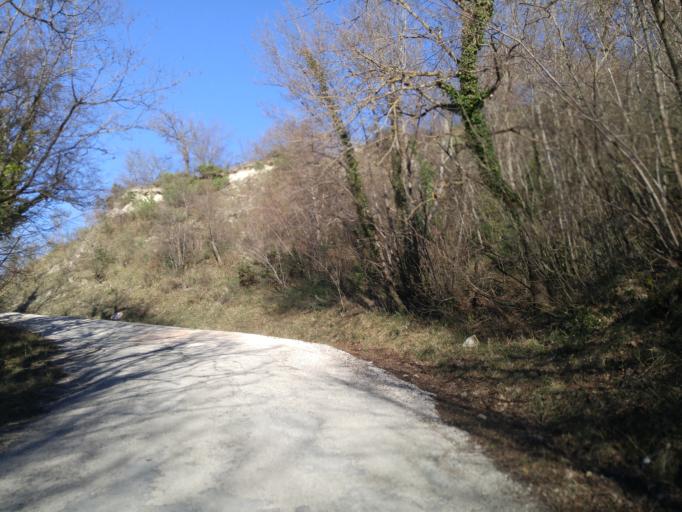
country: IT
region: The Marches
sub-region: Provincia di Pesaro e Urbino
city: Fossombrone
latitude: 43.6613
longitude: 12.7566
